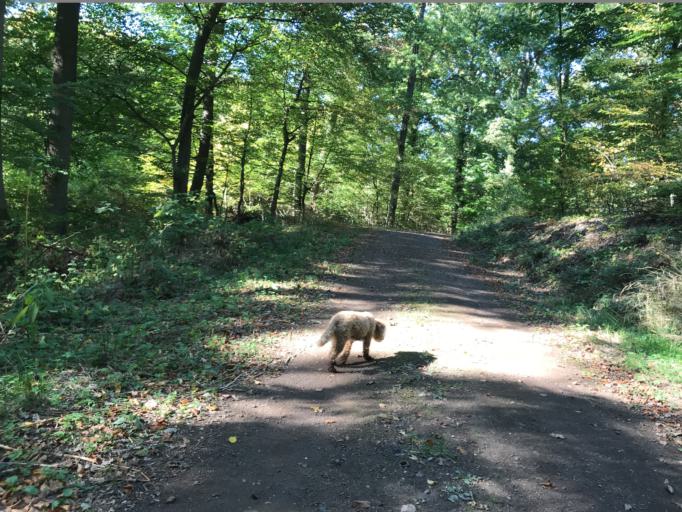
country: DE
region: Rheinland-Pfalz
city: Wolken
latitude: 50.3332
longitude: 7.4442
